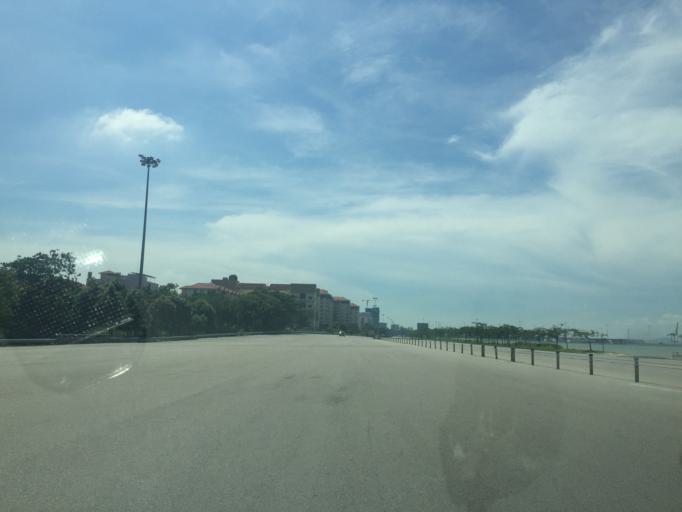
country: MY
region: Penang
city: Permatang Kuching
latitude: 5.4308
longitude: 100.3767
